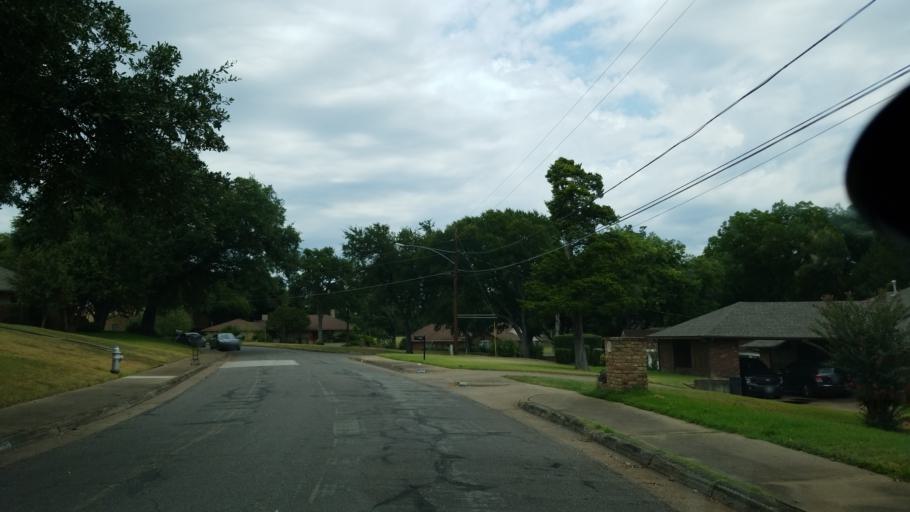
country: US
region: Texas
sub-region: Dallas County
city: Duncanville
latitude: 32.6650
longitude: -96.8542
